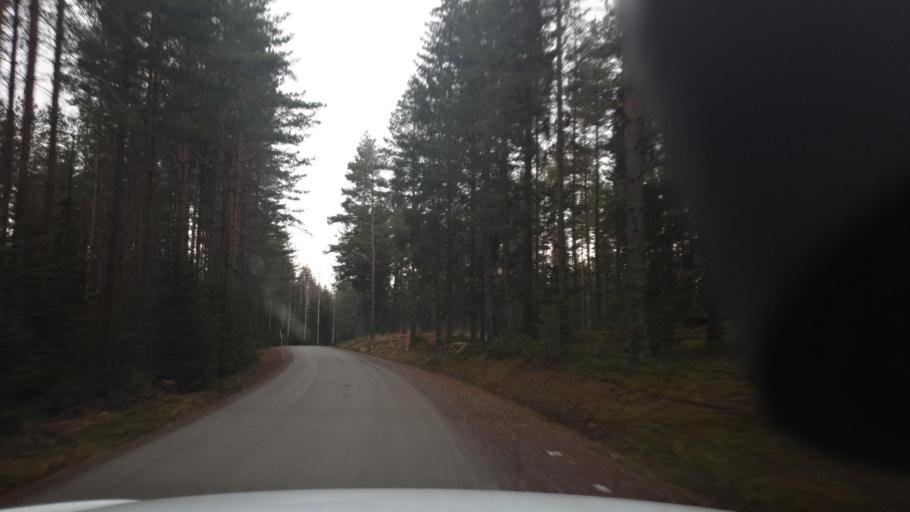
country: SE
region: Vaermland
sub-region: Karlstads Kommun
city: Edsvalla
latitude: 59.6012
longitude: 13.0677
